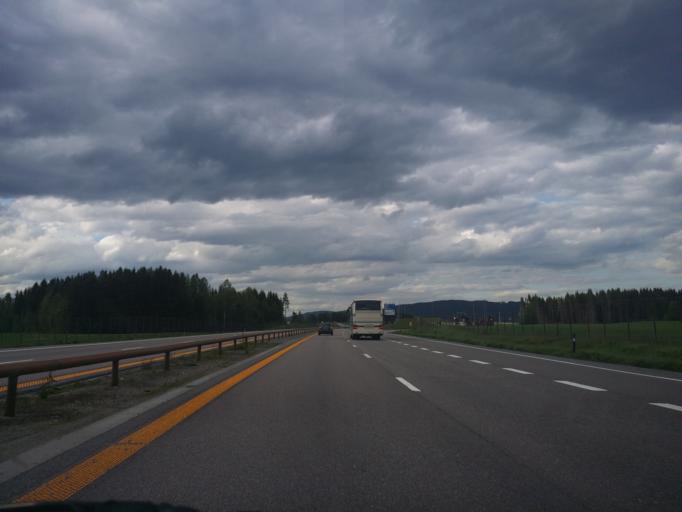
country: NO
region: Akershus
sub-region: Eidsvoll
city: Eidsvoll
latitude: 60.3842
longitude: 11.2115
